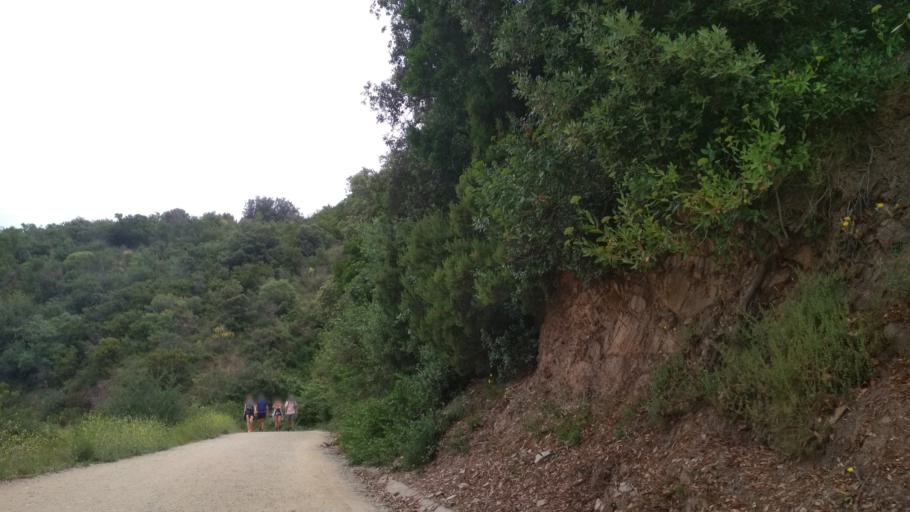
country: ES
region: Catalonia
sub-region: Provincia de Barcelona
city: Nou Barris
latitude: 41.4517
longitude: 2.1638
